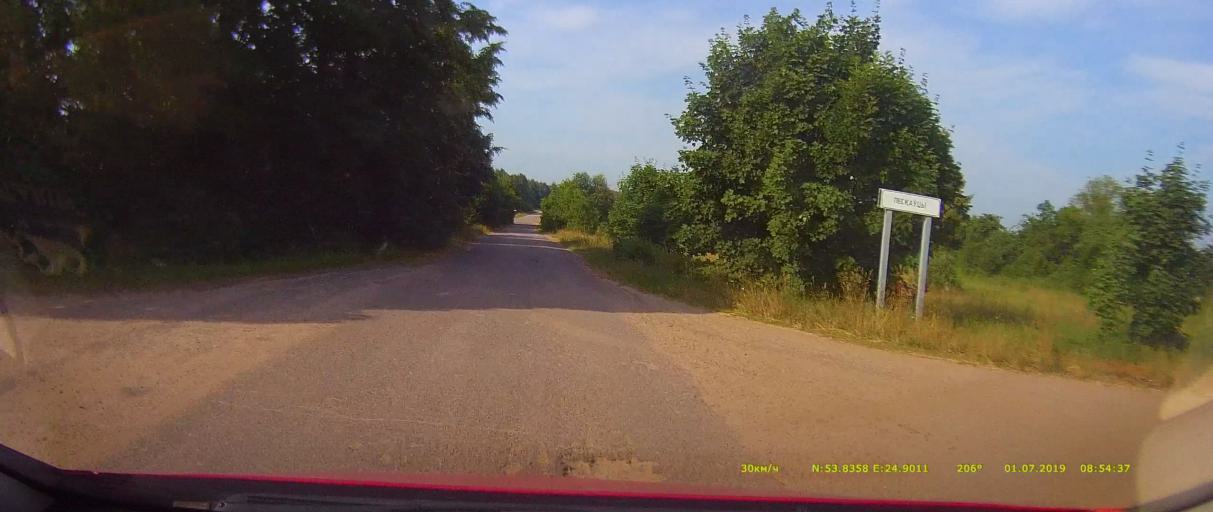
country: BY
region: Grodnenskaya
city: Shchuchin
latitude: 53.8359
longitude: 24.9013
